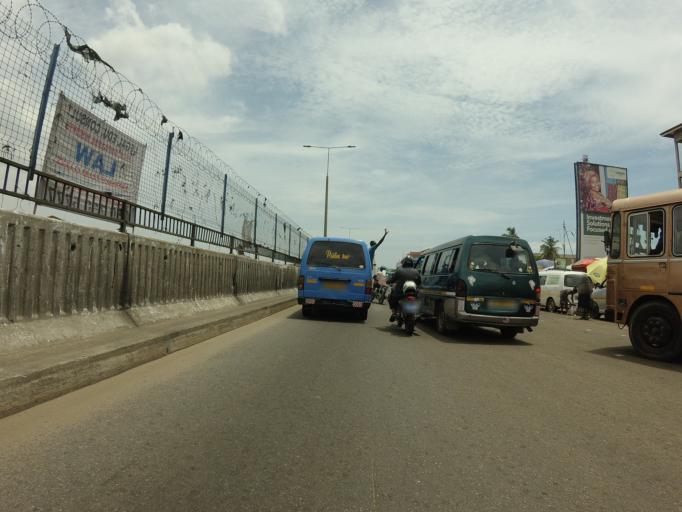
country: GH
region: Greater Accra
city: Accra
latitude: 5.5652
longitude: -0.2357
